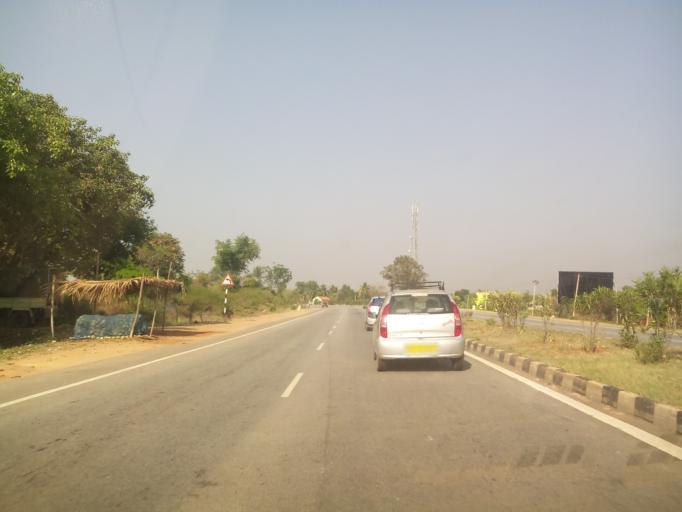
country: IN
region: Karnataka
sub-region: Tumkur
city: Kunigal
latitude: 13.0471
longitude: 77.1427
